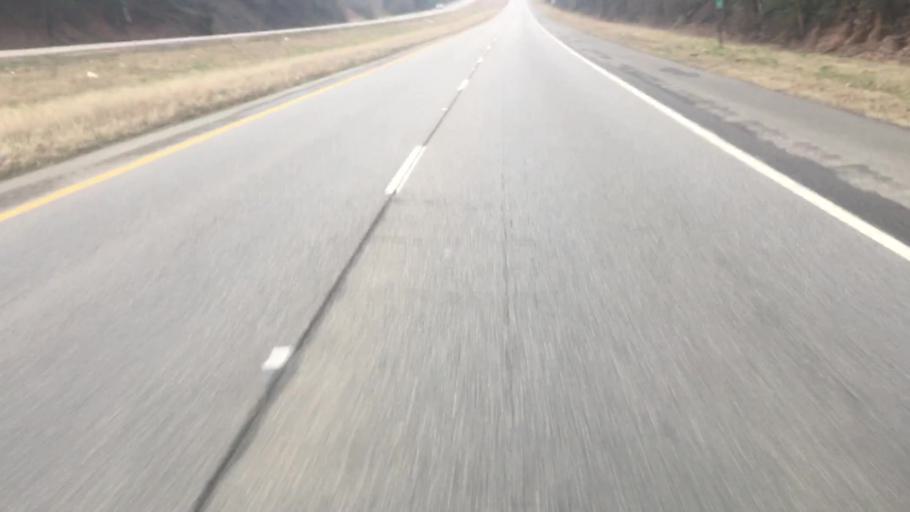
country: US
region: Alabama
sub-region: Walker County
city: Sumiton
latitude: 33.7714
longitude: -87.0727
